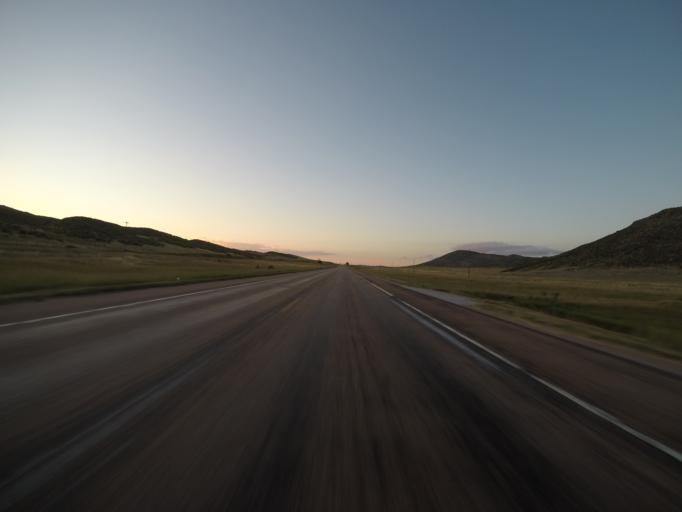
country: US
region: Colorado
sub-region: Larimer County
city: Laporte
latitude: 40.7359
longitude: -105.1710
